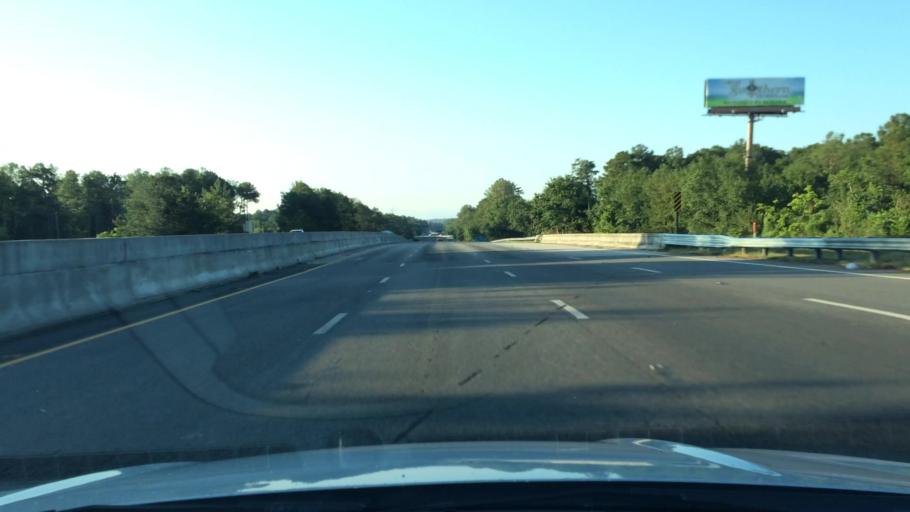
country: US
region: South Carolina
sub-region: Lexington County
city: Springdale
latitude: 33.9777
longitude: -81.1063
